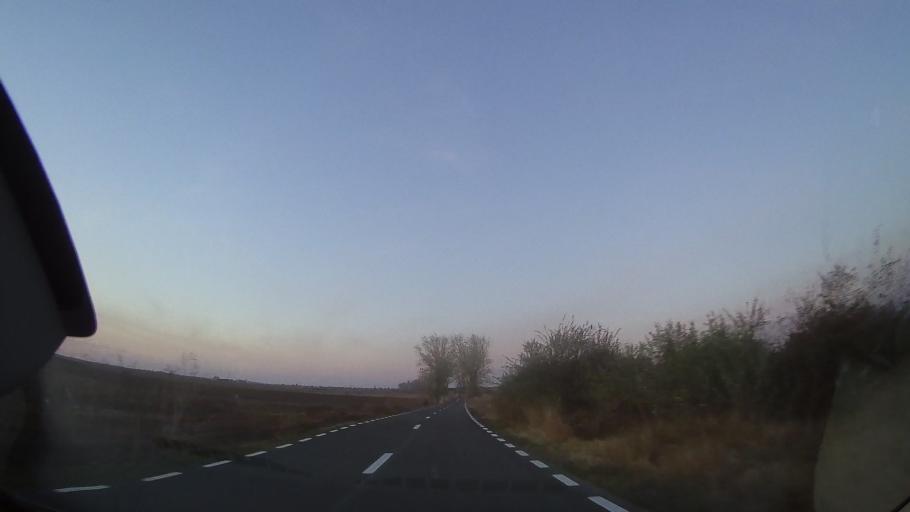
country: RO
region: Constanta
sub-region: Comuna Cobadin
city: Cobadin
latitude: 44.0373
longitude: 28.2586
